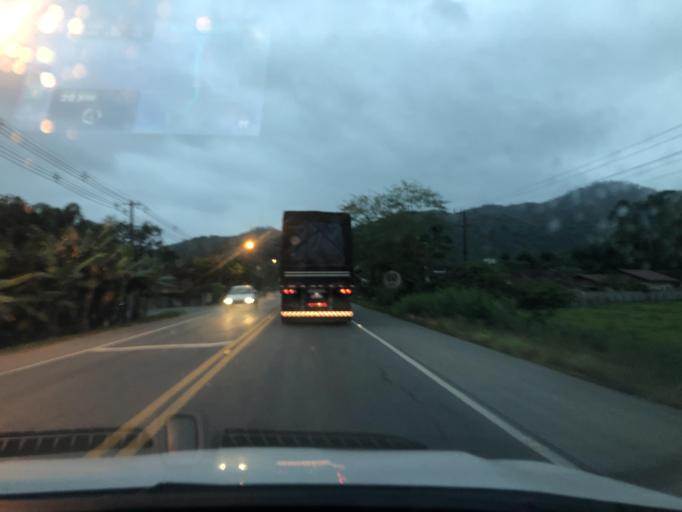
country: BR
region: Santa Catarina
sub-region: Pomerode
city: Pomerode
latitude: -26.7620
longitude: -49.0765
